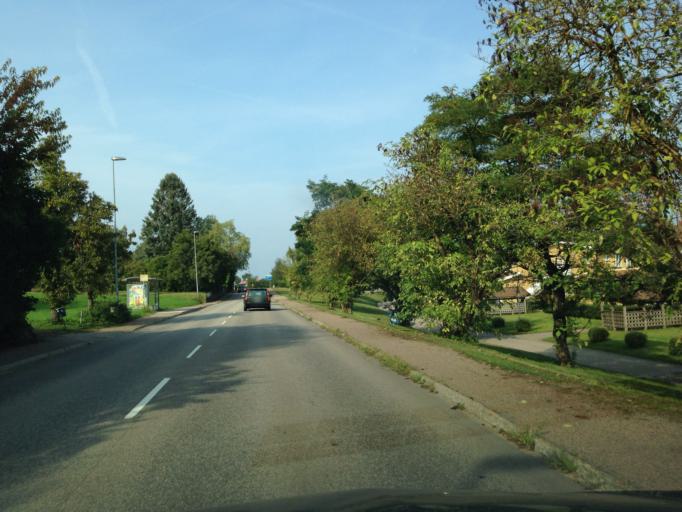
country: SE
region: Skane
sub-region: Bastads Kommun
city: Bastad
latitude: 56.4231
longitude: 12.8451
